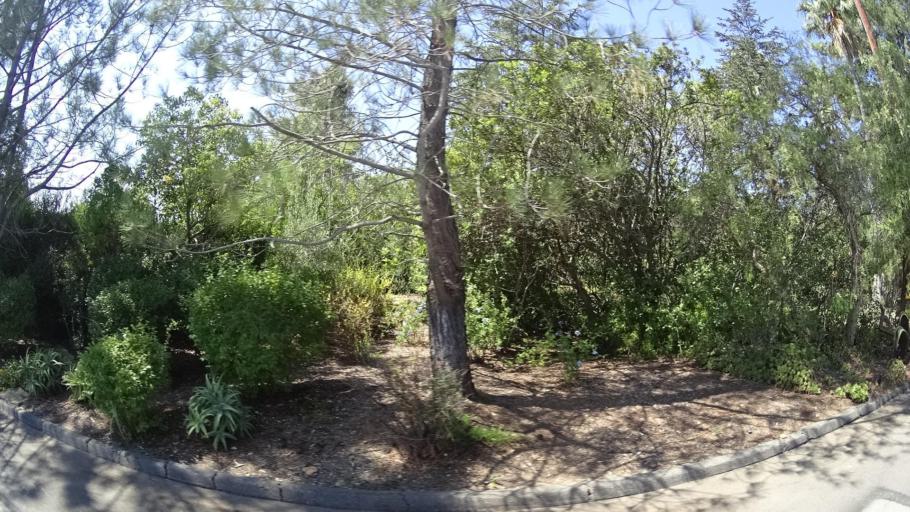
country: US
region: California
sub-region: San Diego County
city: Fairbanks Ranch
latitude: 33.0147
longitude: -117.1790
